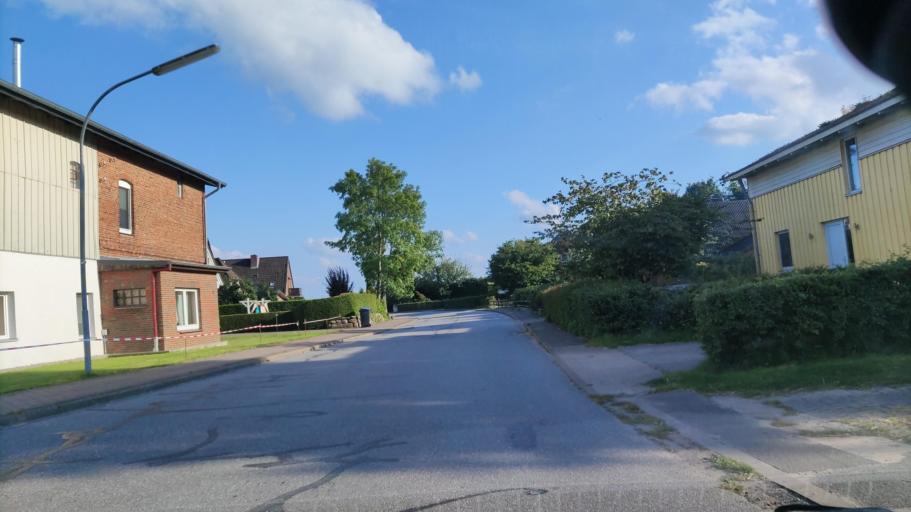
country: DE
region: Schleswig-Holstein
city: Sarlhusen
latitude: 54.0221
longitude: 9.7945
